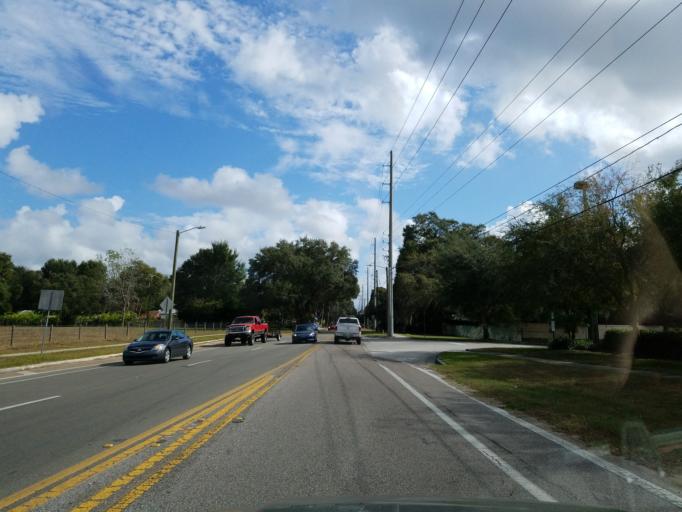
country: US
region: Florida
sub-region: Hillsborough County
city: Bloomingdale
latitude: 27.8936
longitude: -82.2412
